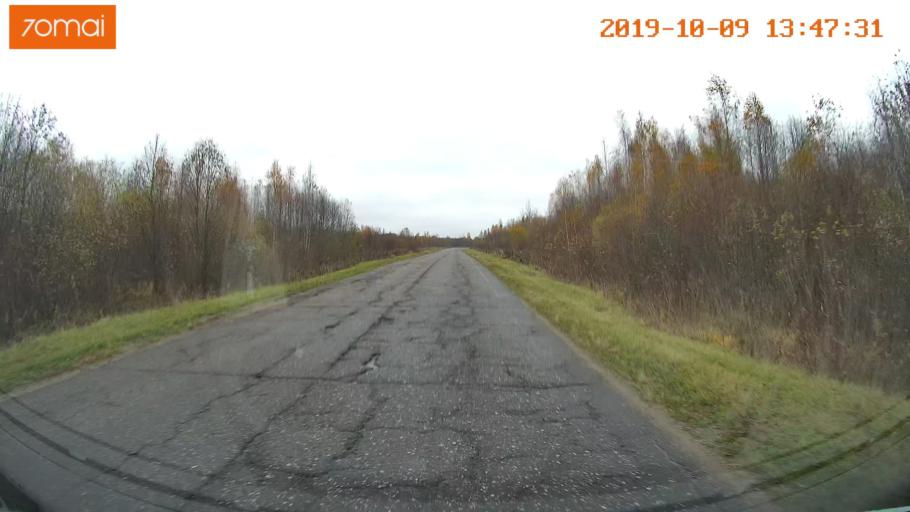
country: RU
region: Kostroma
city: Buy
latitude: 58.3927
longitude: 41.2250
